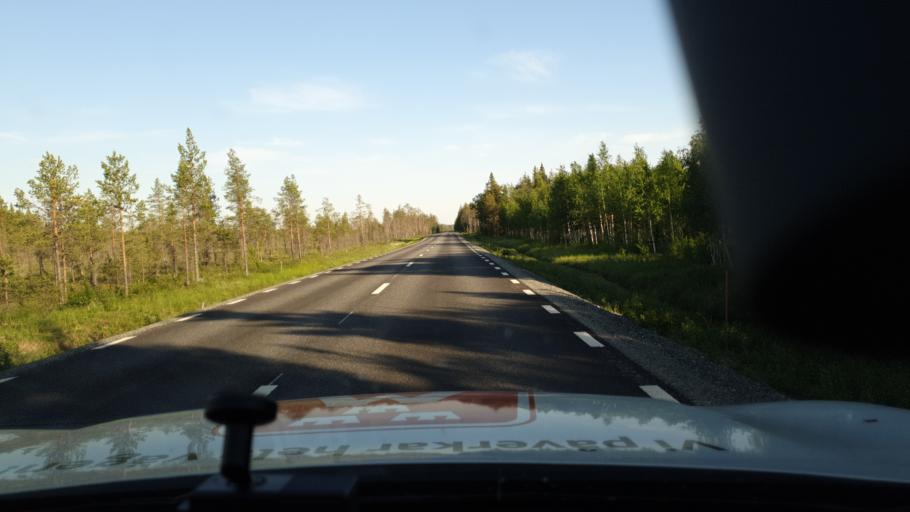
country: SE
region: Vaesterbotten
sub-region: Lycksele Kommun
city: Lycksele
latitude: 64.3610
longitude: 18.5982
